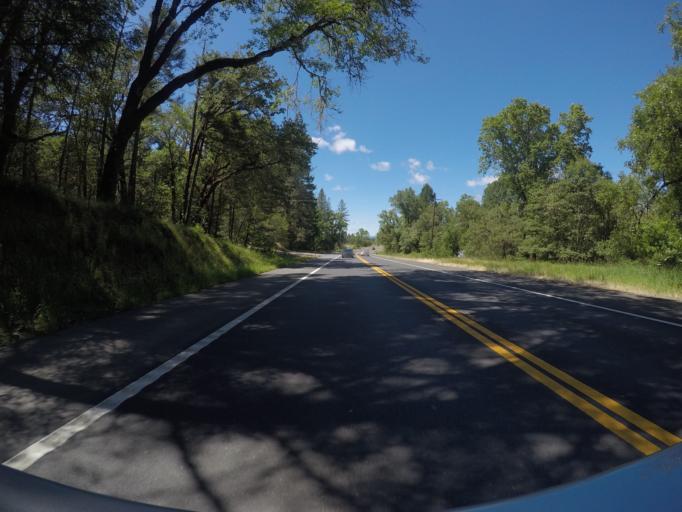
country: US
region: California
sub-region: Mendocino County
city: Laytonville
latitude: 39.6459
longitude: -123.4754
